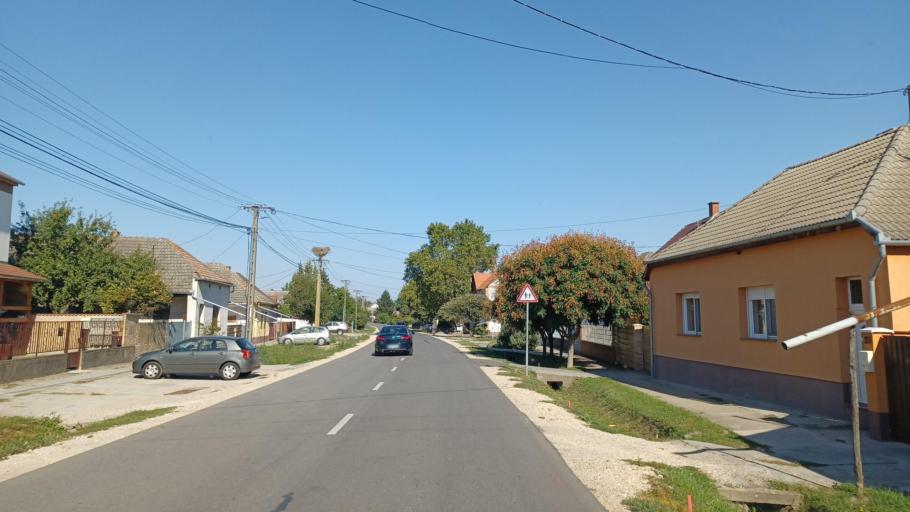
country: HU
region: Tolna
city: Nemetker
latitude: 46.7190
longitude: 18.7625
